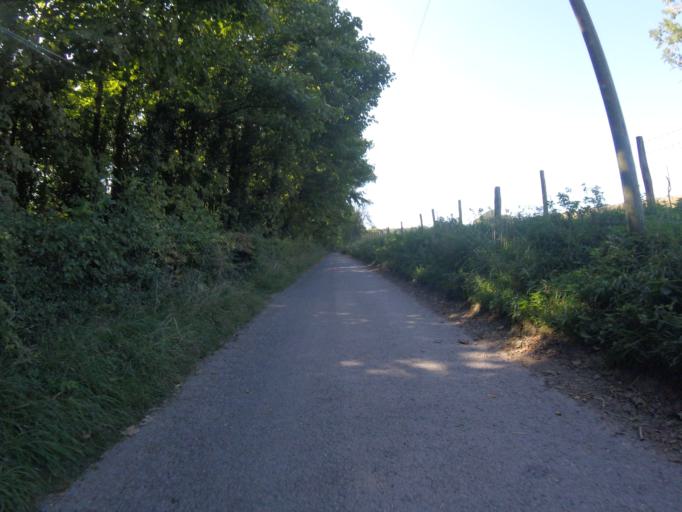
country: GB
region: England
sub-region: Brighton and Hove
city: Brighton
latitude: 50.8730
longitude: -0.1092
